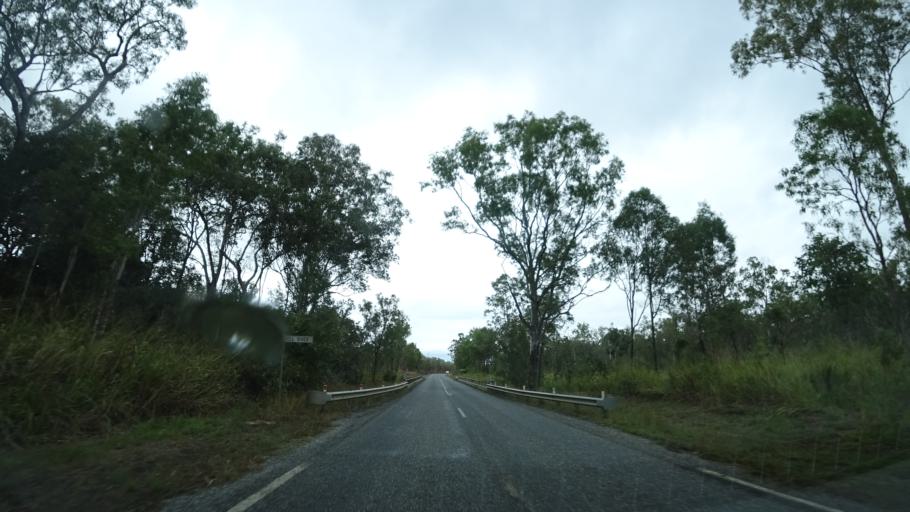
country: AU
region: Queensland
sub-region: Tablelands
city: Mareeba
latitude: -16.7336
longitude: 145.3513
